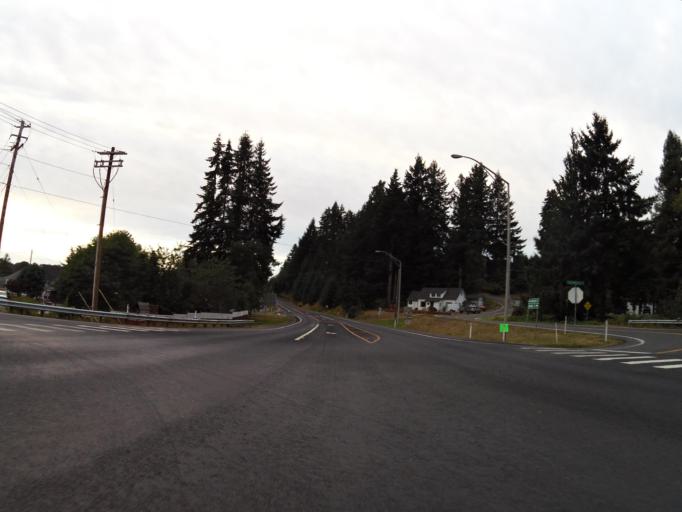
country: US
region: Washington
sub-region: Wahkiakum County
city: Cathlamet
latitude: 46.2046
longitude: -123.3821
